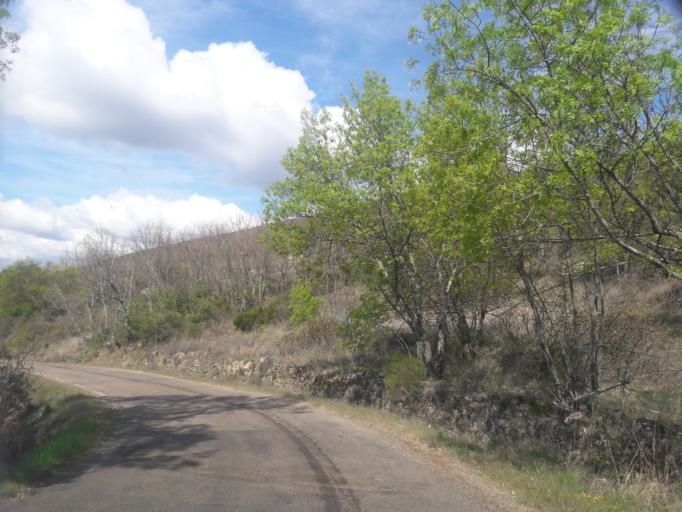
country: ES
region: Castille and Leon
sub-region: Provincia de Salamanca
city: San Esteban de la Sierra
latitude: 40.5078
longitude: -5.8784
